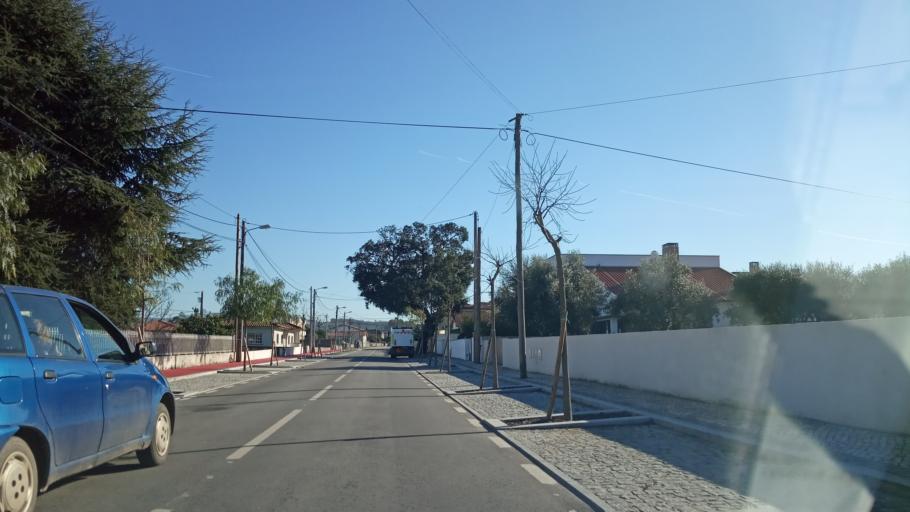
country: PT
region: Aveiro
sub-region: Anadia
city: Anadia
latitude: 40.4319
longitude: -8.4307
